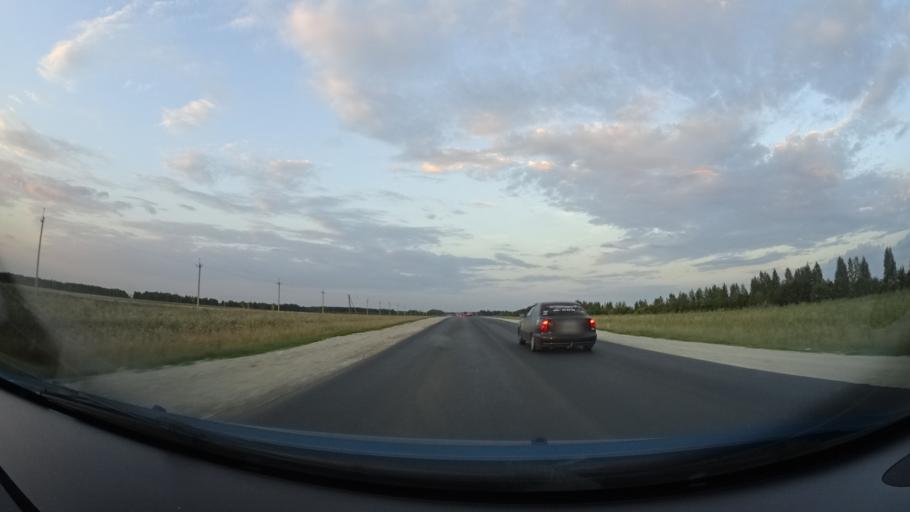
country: RU
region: Tatarstan
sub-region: Bugul'minskiy Rayon
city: Bugul'ma
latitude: 54.2524
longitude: 52.8556
